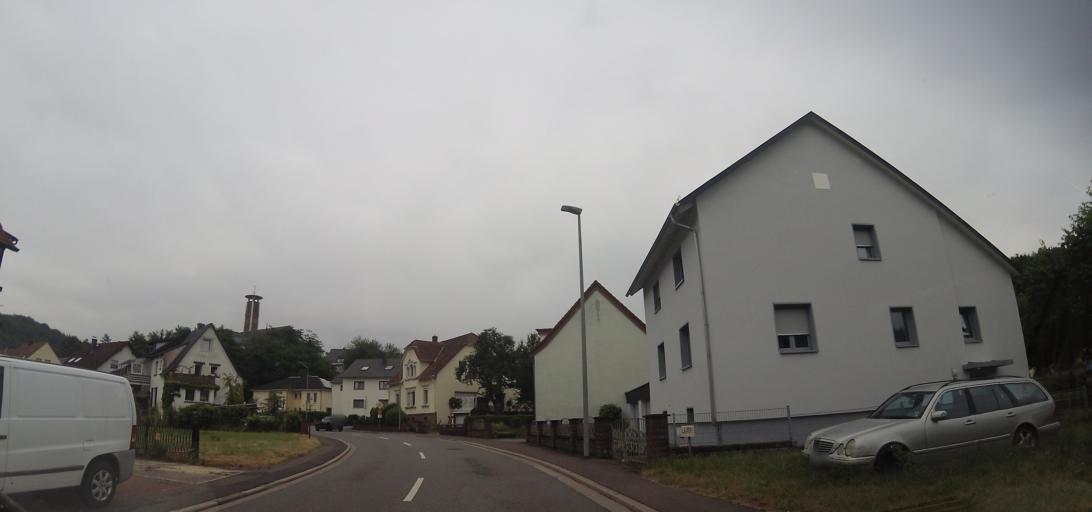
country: DE
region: Saarland
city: Homburg
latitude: 49.2999
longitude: 7.3639
